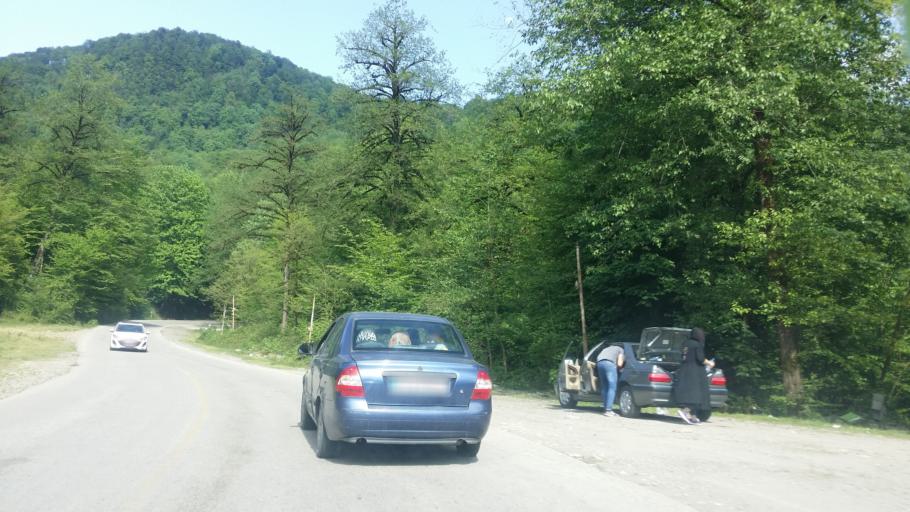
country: IR
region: Mazandaran
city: `Abbasabad
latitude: 36.6479
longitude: 51.1119
